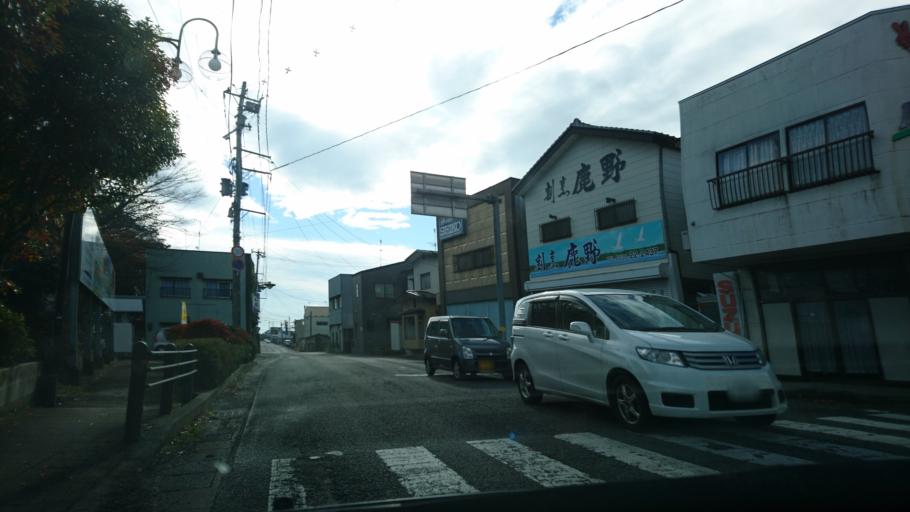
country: JP
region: Miyagi
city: Wakuya
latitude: 38.6850
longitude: 141.1968
